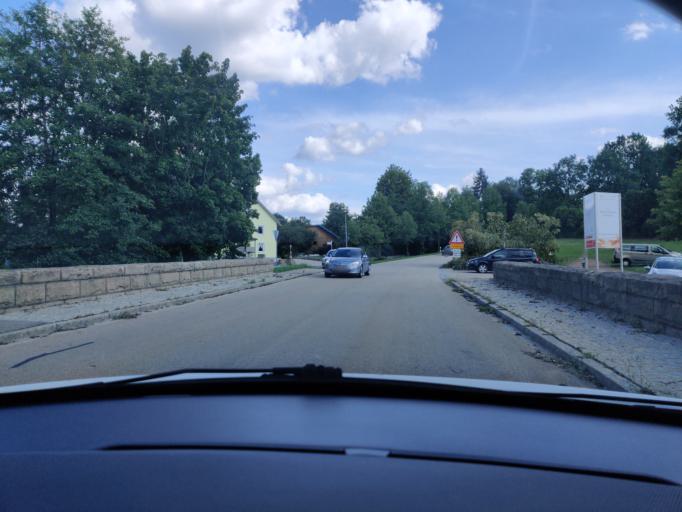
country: DE
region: Bavaria
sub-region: Upper Palatinate
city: Nabburg
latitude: 49.4694
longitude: 12.1869
